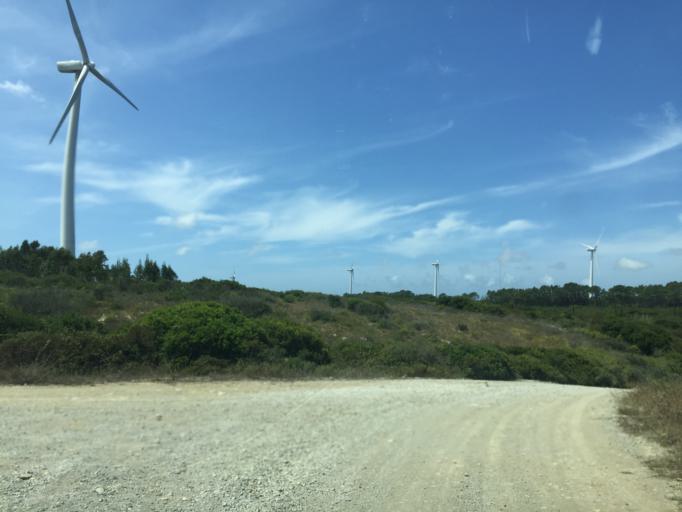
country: PT
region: Leiria
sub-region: Peniche
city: Atouguia da Baleia
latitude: 39.3176
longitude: -9.2598
